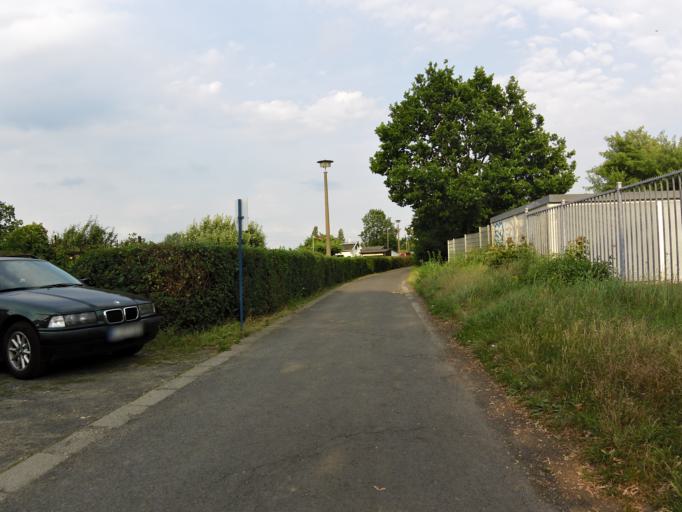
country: DE
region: Saxony
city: Markkleeberg
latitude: 51.3090
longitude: 12.3216
